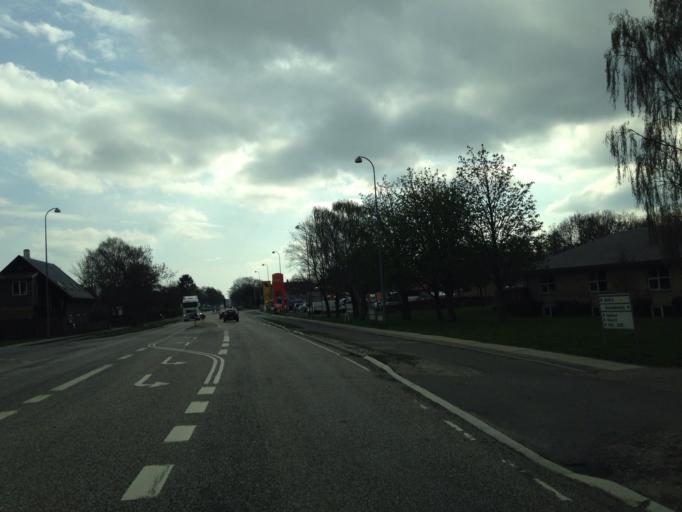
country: DK
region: Capital Region
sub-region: Hoje-Taastrup Kommune
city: Taastrup
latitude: 55.6305
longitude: 12.2838
